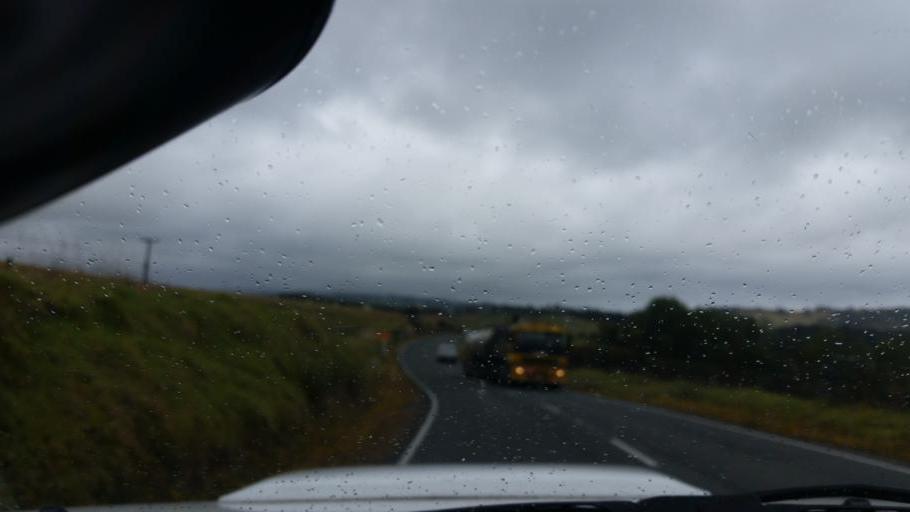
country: NZ
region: Auckland
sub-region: Auckland
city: Wellsford
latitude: -36.1439
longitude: 174.4981
